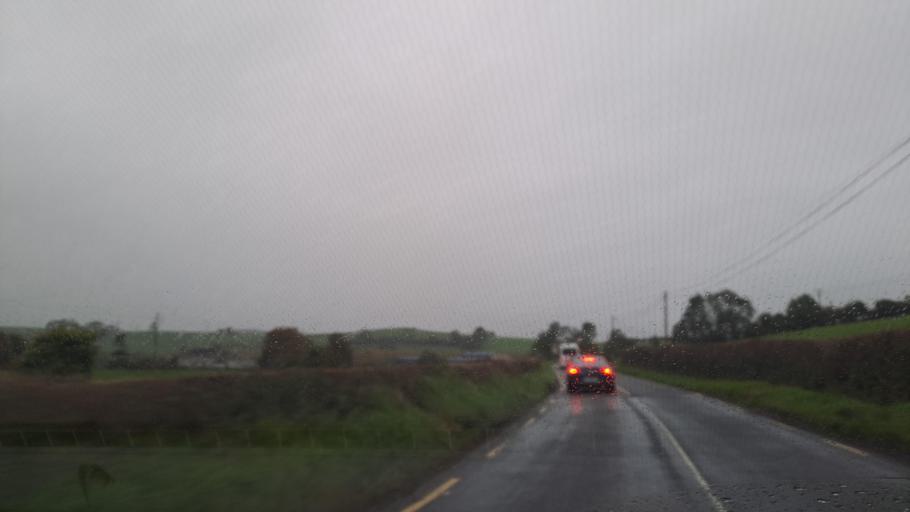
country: IE
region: Ulster
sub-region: County Monaghan
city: Monaghan
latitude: 54.2270
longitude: -6.9529
